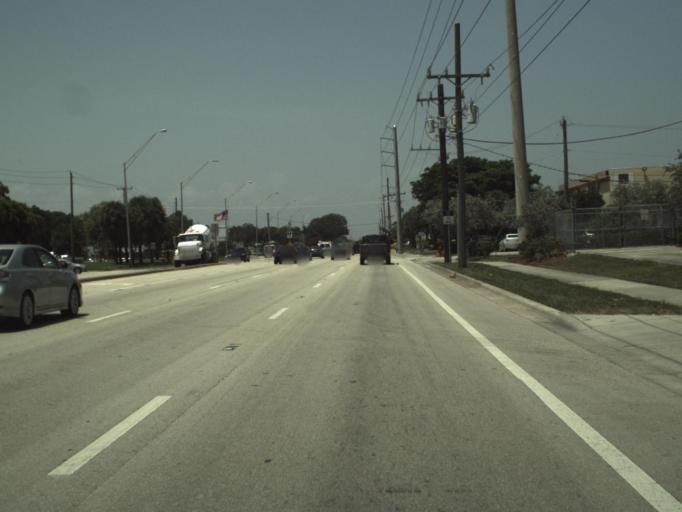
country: US
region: Florida
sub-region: Broward County
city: Coconut Creek
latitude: 26.2477
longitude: -80.1515
